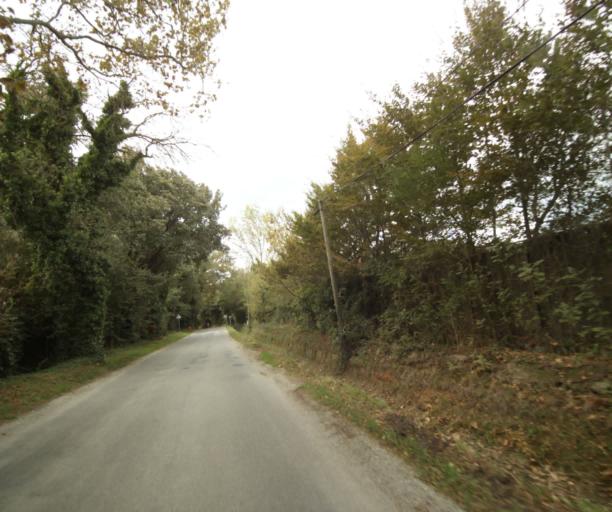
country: FR
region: Languedoc-Roussillon
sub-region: Departement des Pyrenees-Orientales
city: Argelers
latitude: 42.5650
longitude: 3.0310
